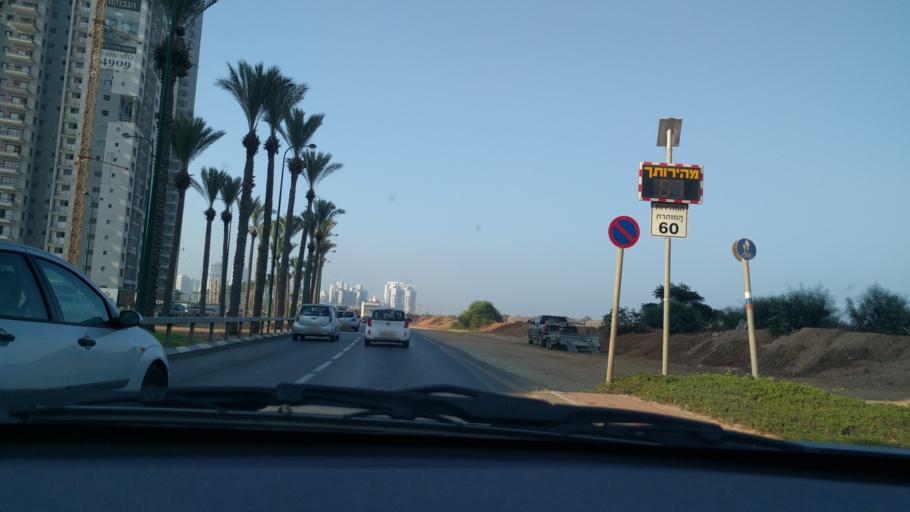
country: IL
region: Central District
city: Netanya
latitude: 32.2943
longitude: 34.8425
